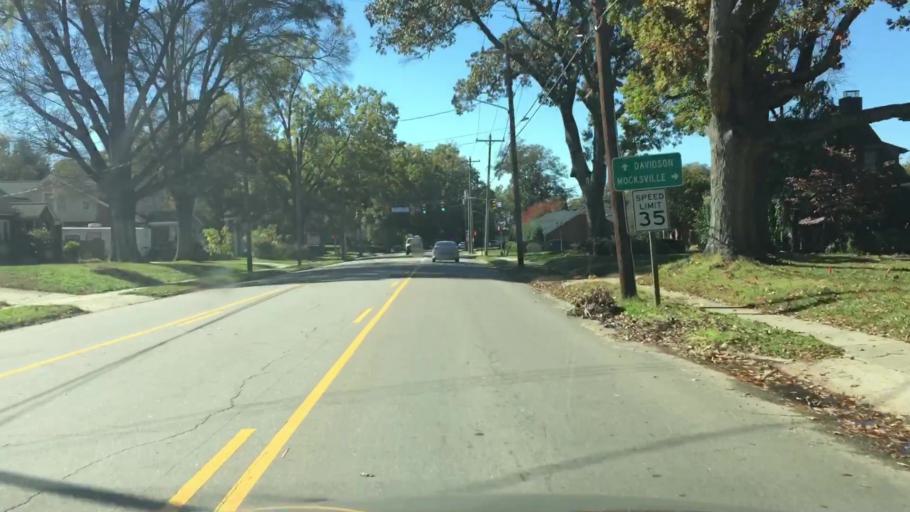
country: US
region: North Carolina
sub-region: Iredell County
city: Mooresville
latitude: 35.5878
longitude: -80.7983
